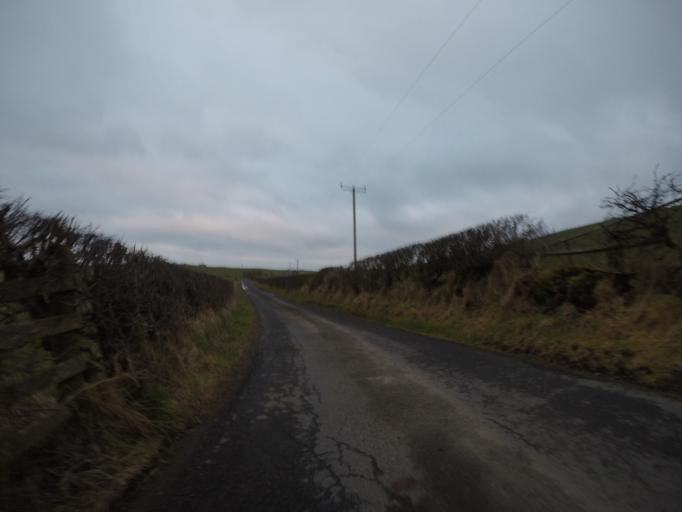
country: GB
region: Scotland
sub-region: North Ayrshire
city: Stevenston
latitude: 55.6866
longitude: -4.7661
